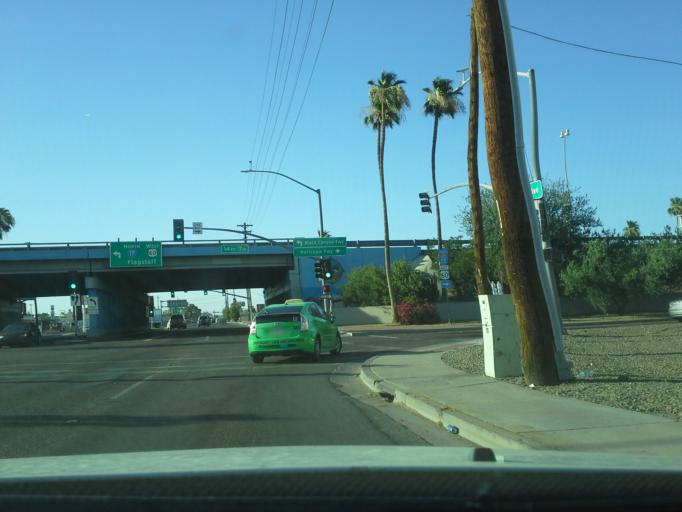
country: US
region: Arizona
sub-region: Maricopa County
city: Phoenix
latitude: 33.4283
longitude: -112.0997
